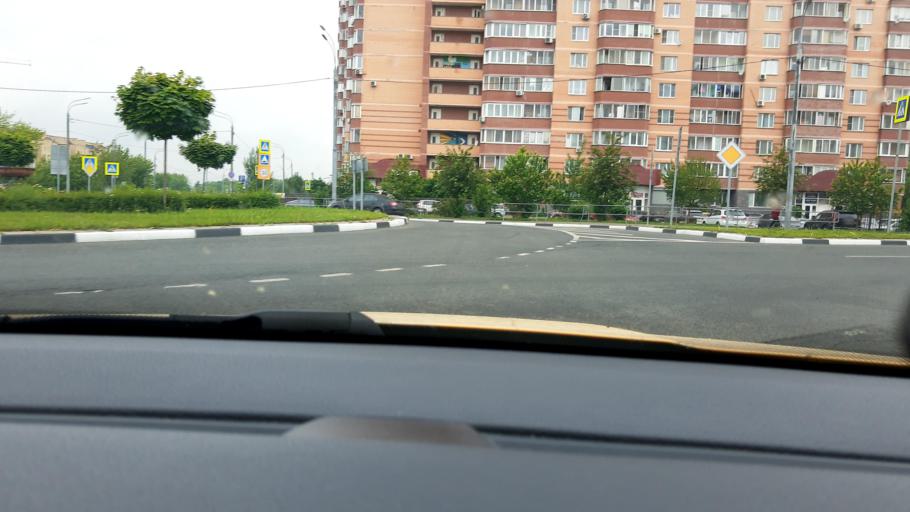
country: RU
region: Moscow
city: Vatutino
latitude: 55.9016
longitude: 37.7038
